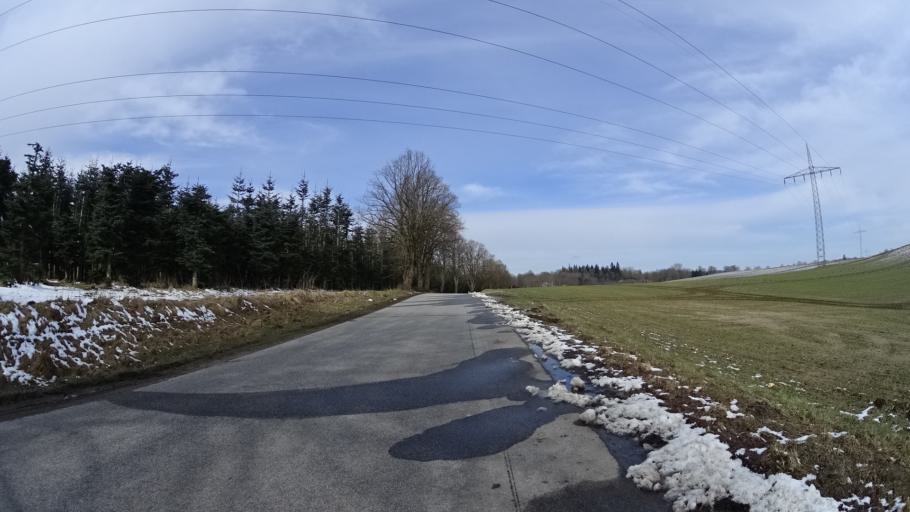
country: DE
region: Schleswig-Holstein
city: Stolpe
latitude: 54.1506
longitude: 10.2337
